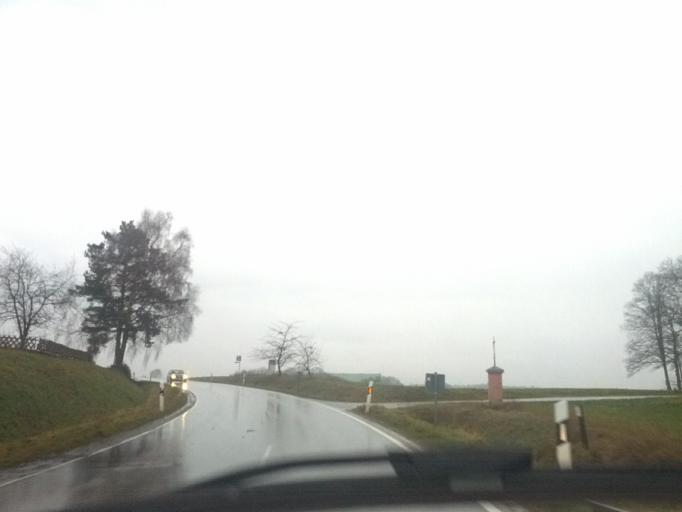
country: DE
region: Baden-Wuerttemberg
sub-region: Tuebingen Region
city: Erlenmoos
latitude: 48.0515
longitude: 9.9790
